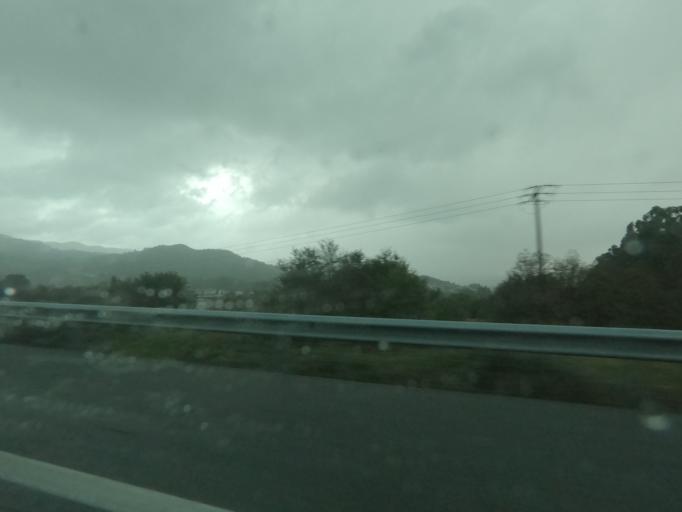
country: ES
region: Galicia
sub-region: Provincia de Pontevedra
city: Marin
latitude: 42.3577
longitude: -8.6408
